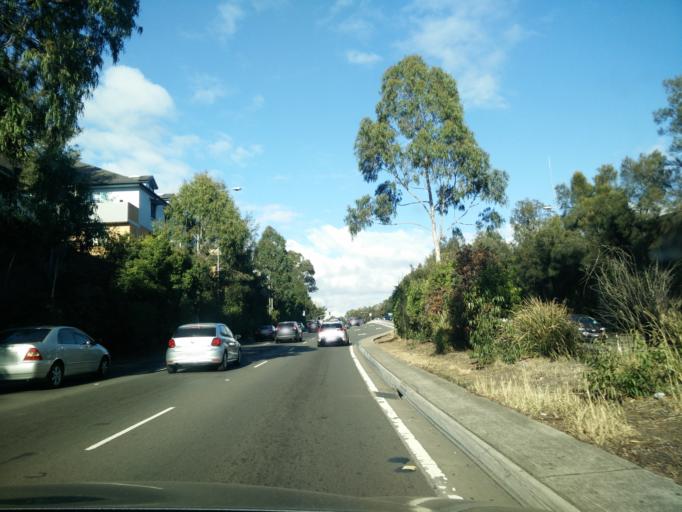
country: AU
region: New South Wales
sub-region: Strathfield
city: Homebush
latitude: -33.8660
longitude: 151.0654
